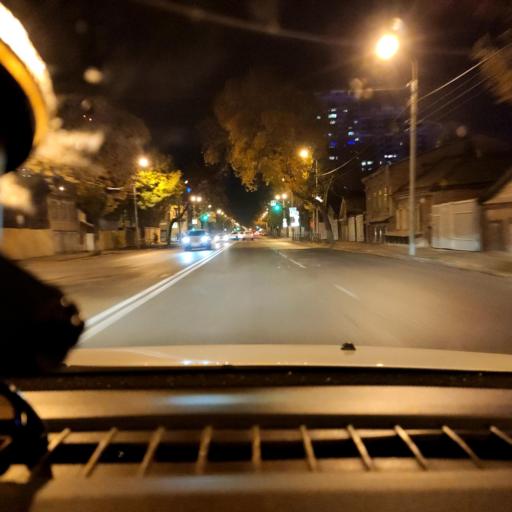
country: RU
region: Samara
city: Samara
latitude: 53.2042
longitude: 50.1214
